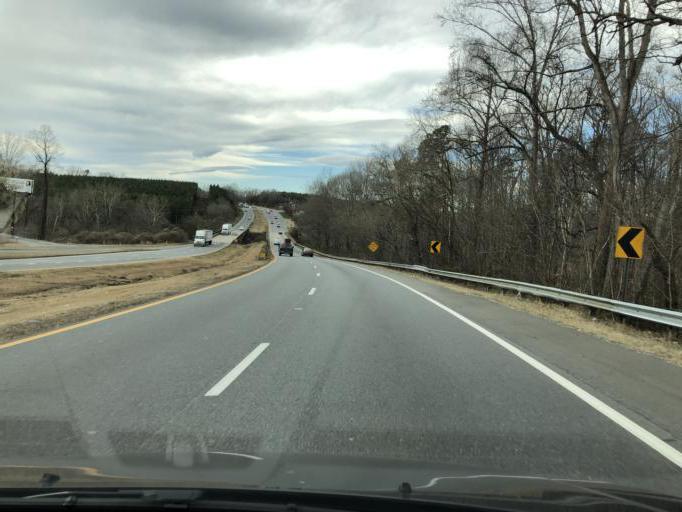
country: US
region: North Carolina
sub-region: Cleveland County
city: Shelby
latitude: 35.2944
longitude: -81.5682
